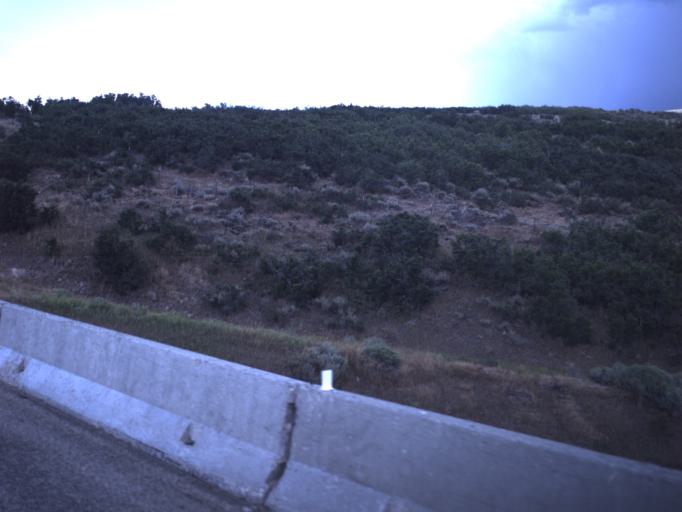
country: US
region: Utah
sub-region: Wasatch County
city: Heber
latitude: 40.5904
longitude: -111.3780
